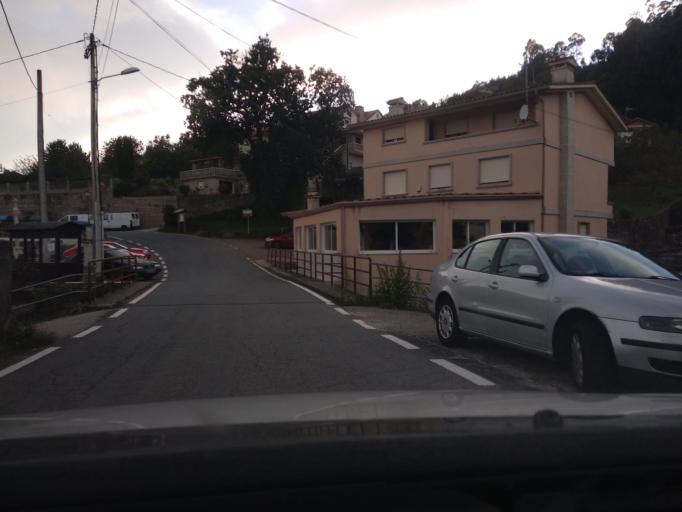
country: ES
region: Galicia
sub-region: Provincia de Pontevedra
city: Moana
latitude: 42.2894
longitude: -8.6849
